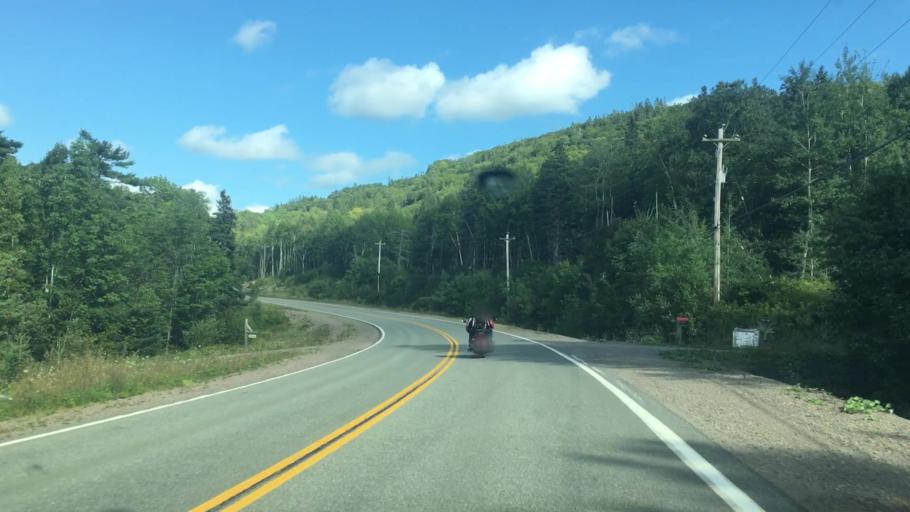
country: CA
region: Nova Scotia
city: Sydney
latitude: 45.8497
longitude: -60.6413
